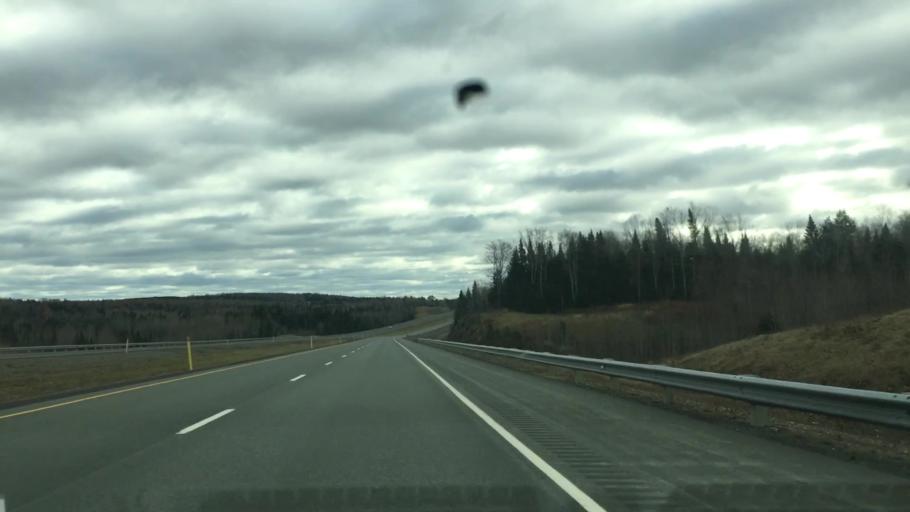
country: CA
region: New Brunswick
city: Florenceville-Bristol
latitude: 46.5437
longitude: -67.7189
